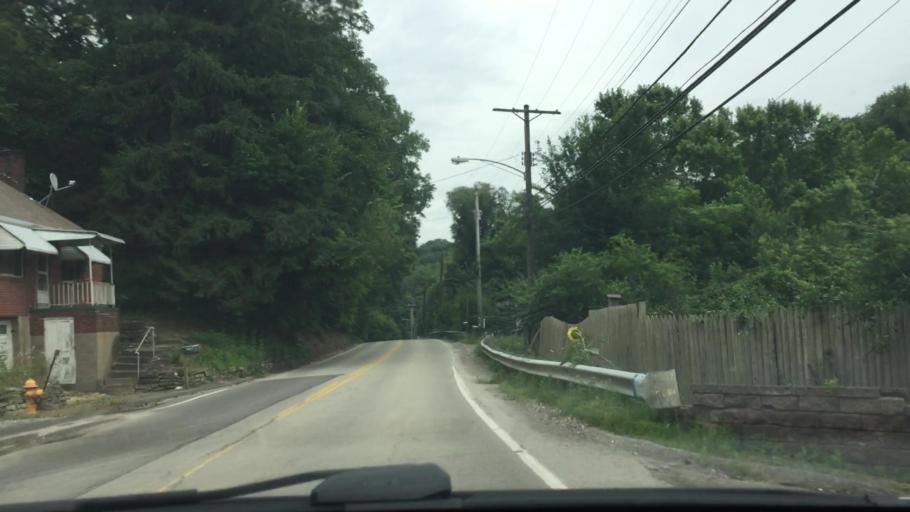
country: US
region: Pennsylvania
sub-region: Allegheny County
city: Rennerdale
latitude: 40.3753
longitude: -80.1353
